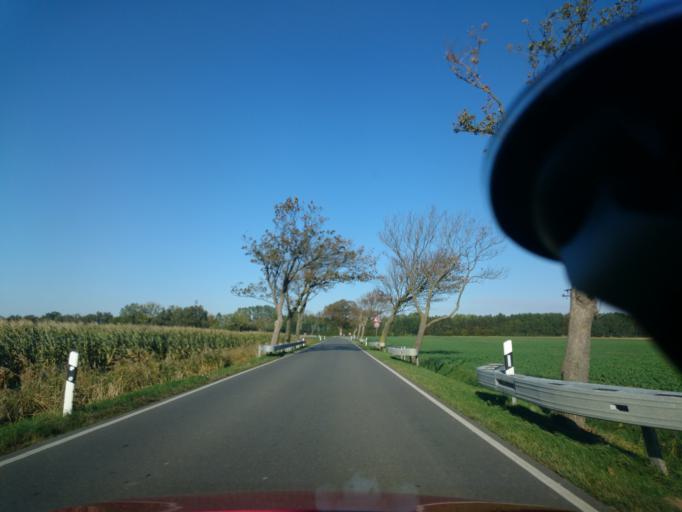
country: DE
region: Mecklenburg-Vorpommern
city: Saal
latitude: 54.3021
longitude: 12.5084
